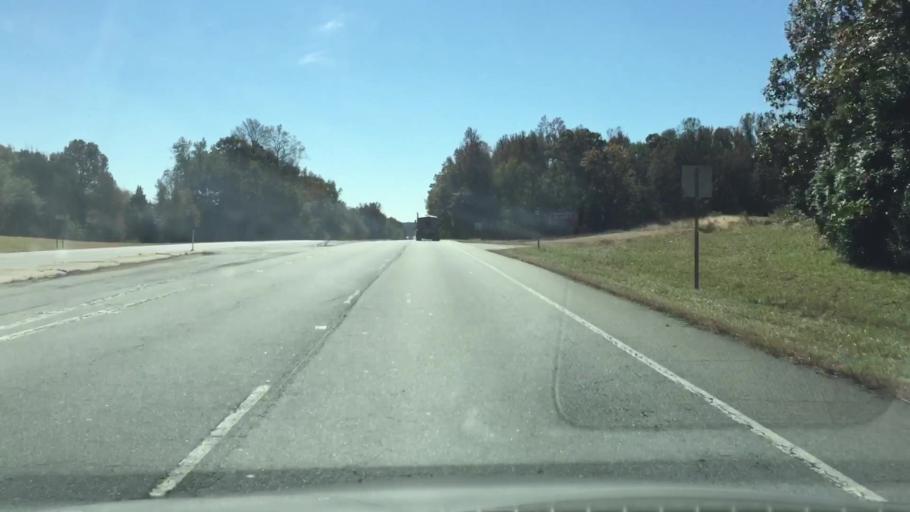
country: US
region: North Carolina
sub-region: Guilford County
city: McLeansville
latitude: 36.1984
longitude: -79.6979
